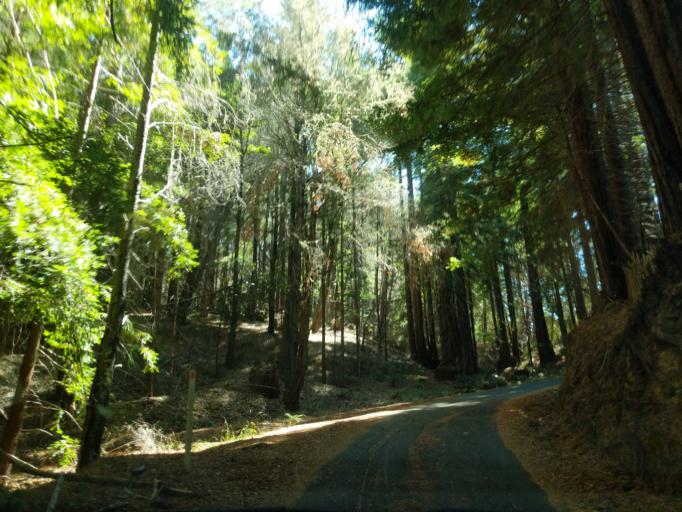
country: US
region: California
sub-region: Sonoma County
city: Monte Rio
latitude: 38.5250
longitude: -123.2354
